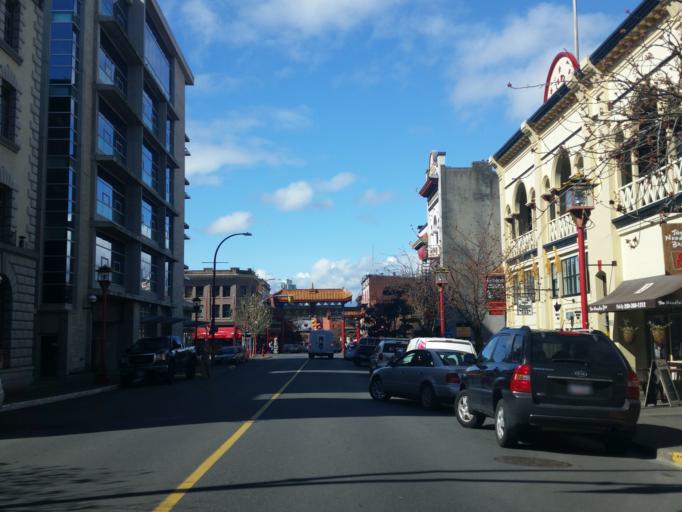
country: CA
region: British Columbia
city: Victoria
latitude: 48.4295
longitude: -123.3657
